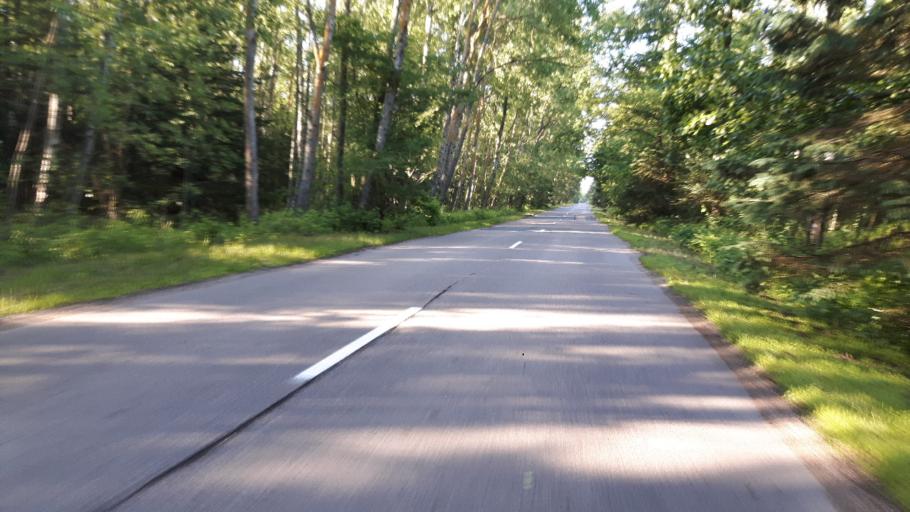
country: LT
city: Nida
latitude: 55.2315
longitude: 20.9031
